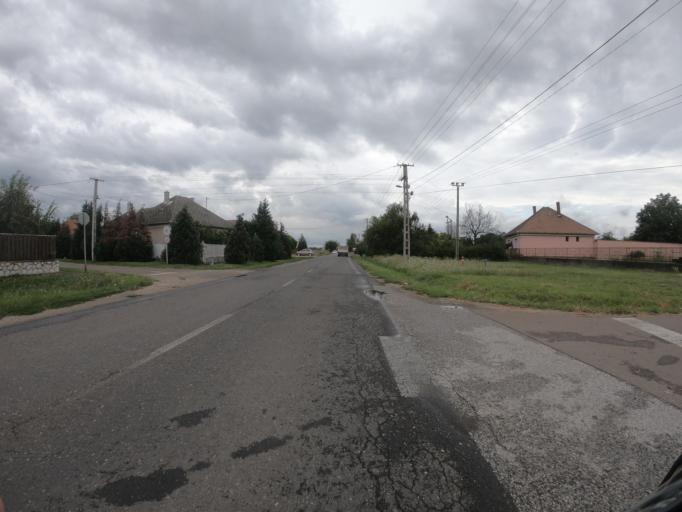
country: HU
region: Borsod-Abauj-Zemplen
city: Mezokovesd
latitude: 47.8047
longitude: 20.5927
